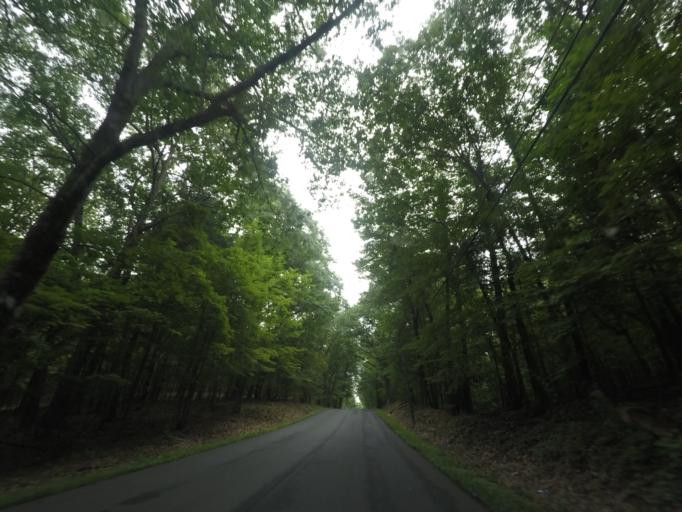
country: US
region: New York
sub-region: Rensselaer County
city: Nassau
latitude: 42.5009
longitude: -73.6053
